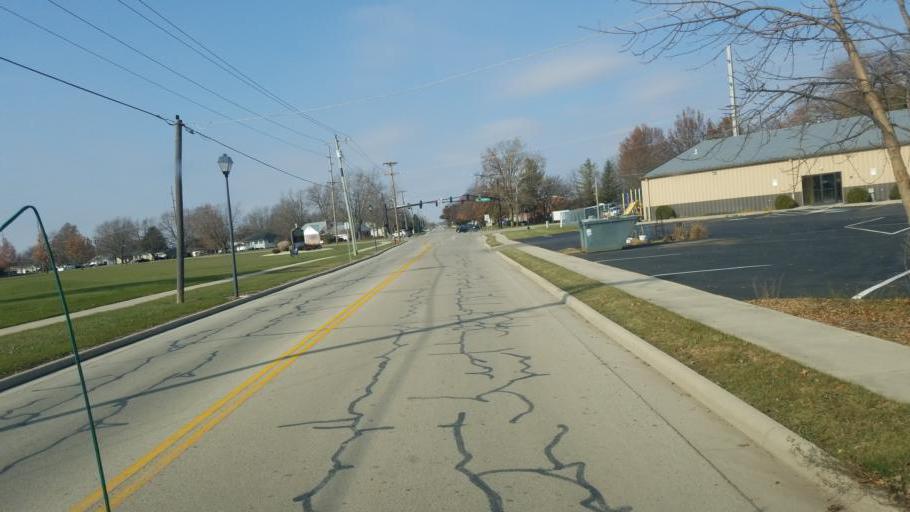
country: US
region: Ohio
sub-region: Mercer County
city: Celina
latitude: 40.5594
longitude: -84.5797
